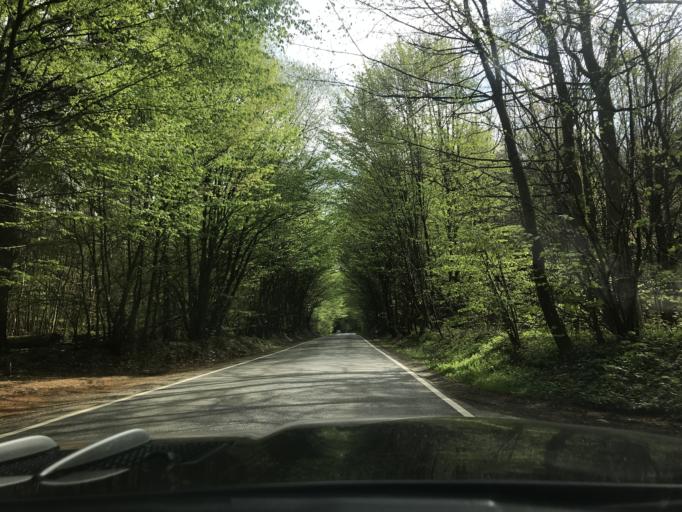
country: DE
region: Schleswig-Holstein
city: Ratekau
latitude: 53.9244
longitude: 10.7876
